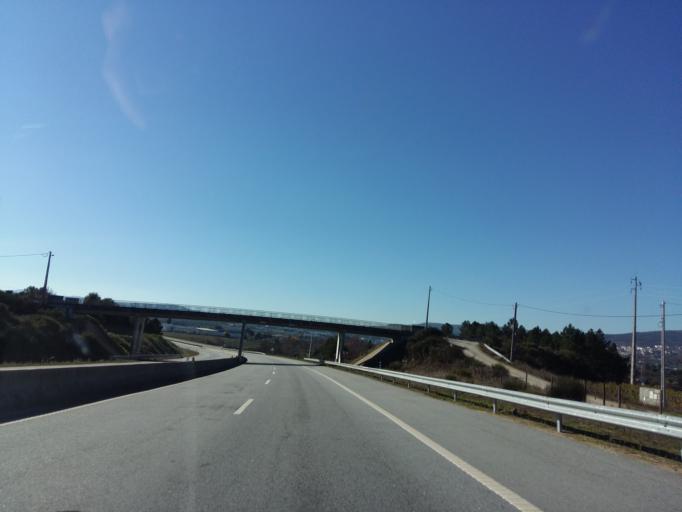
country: PT
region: Castelo Branco
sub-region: Covilha
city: Covilha
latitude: 40.2422
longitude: -7.4777
